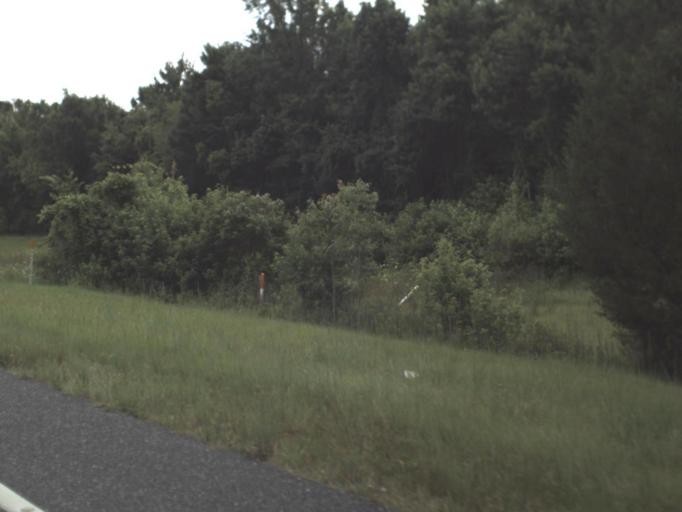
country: US
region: Florida
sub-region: Levy County
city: Williston Highlands
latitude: 29.2572
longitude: -82.7255
